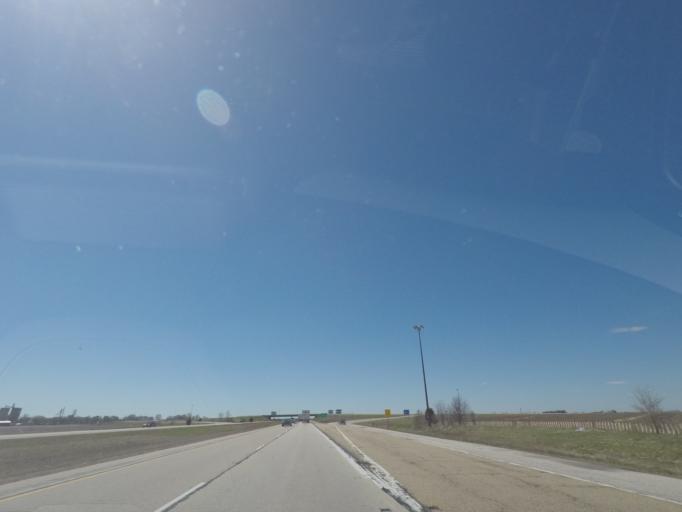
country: US
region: Illinois
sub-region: McLean County
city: Hudson
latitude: 40.5755
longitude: -88.8972
